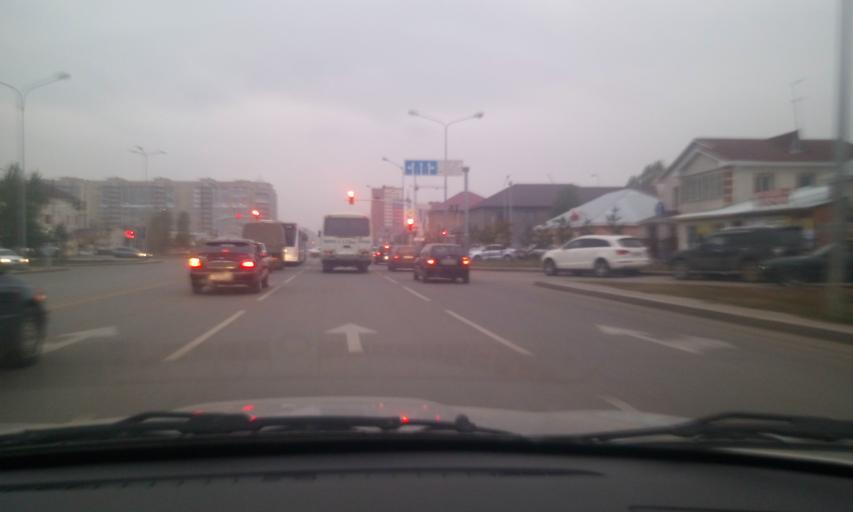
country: KZ
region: Astana Qalasy
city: Astana
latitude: 51.1347
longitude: 71.4931
